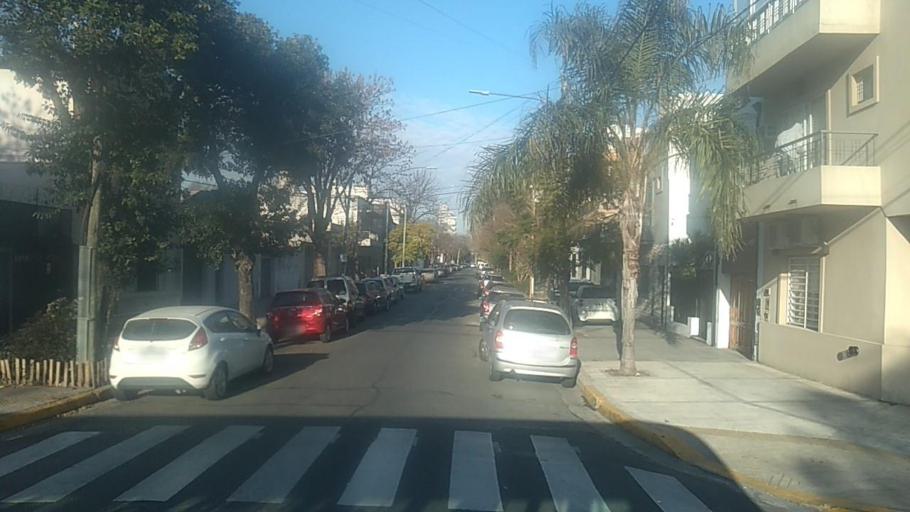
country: AR
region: Buenos Aires F.D.
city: Villa Santa Rita
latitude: -34.6203
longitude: -58.5113
